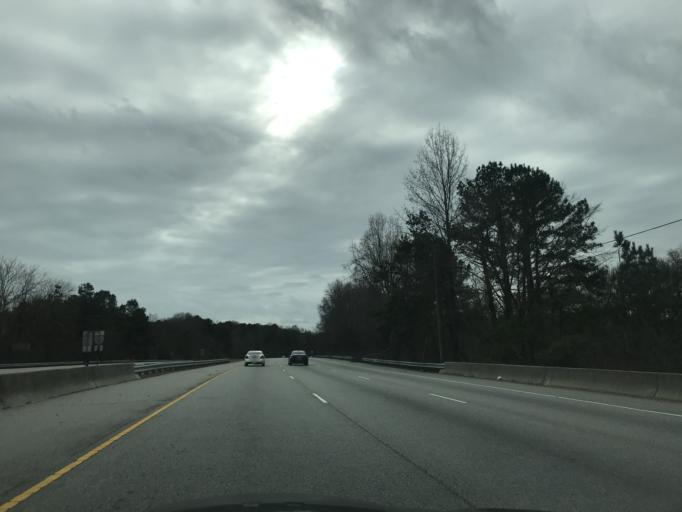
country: US
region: North Carolina
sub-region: Wake County
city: Raleigh
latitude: 35.7499
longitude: -78.6365
